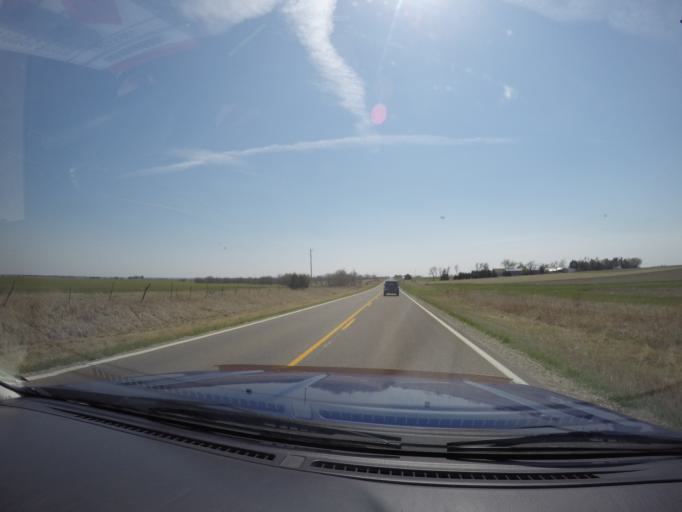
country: US
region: Kansas
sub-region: Morris County
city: Council Grove
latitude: 38.8230
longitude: -96.5013
